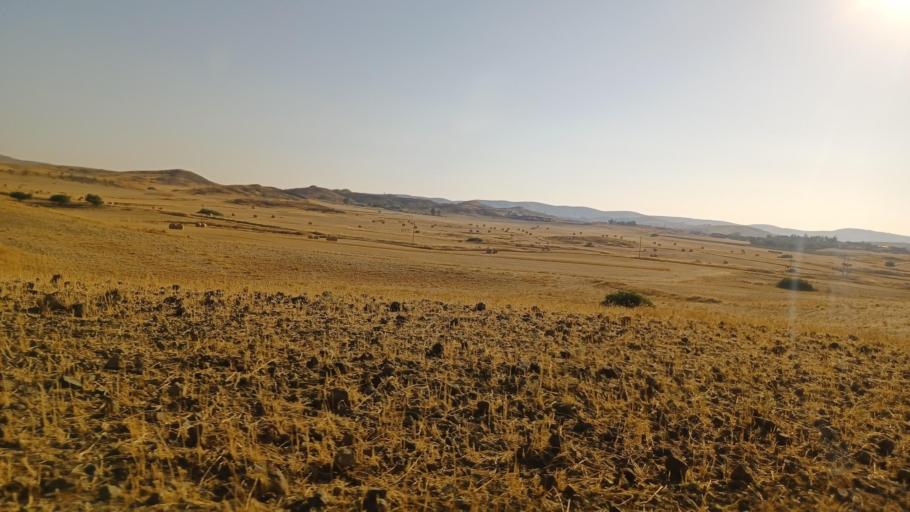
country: CY
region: Larnaka
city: Troulloi
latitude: 35.0126
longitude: 33.5967
